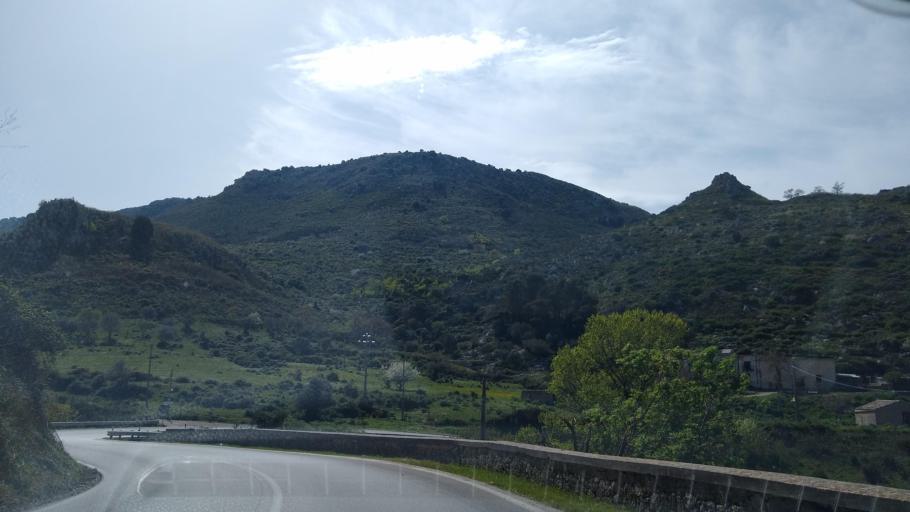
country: IT
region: Sicily
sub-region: Palermo
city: Pioppo
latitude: 38.0411
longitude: 13.2006
